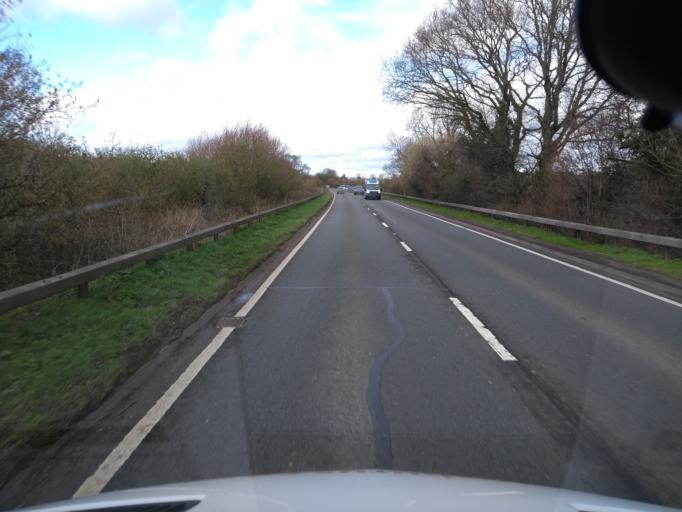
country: GB
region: England
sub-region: Somerset
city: Stoke-sub-Hamdon
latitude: 50.9503
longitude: -2.6978
